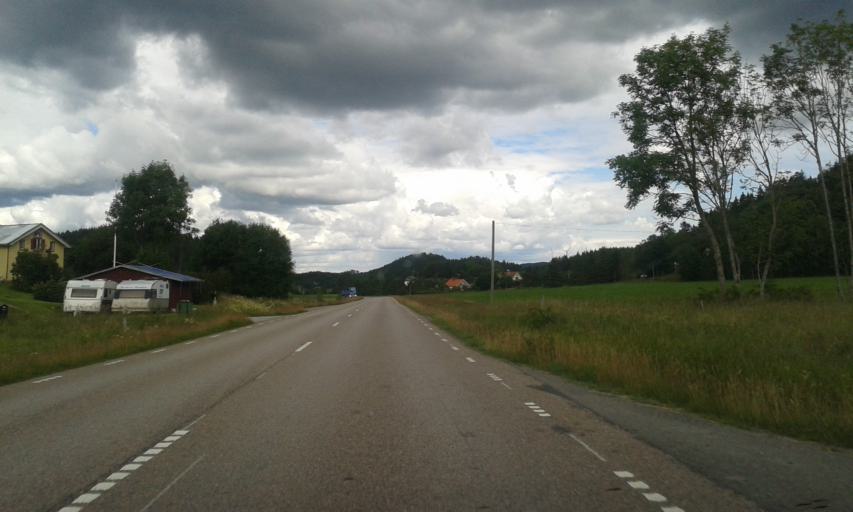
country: SE
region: Vaestra Goetaland
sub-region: Lilla Edets Kommun
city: Lilla Edet
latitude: 58.0928
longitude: 12.1186
